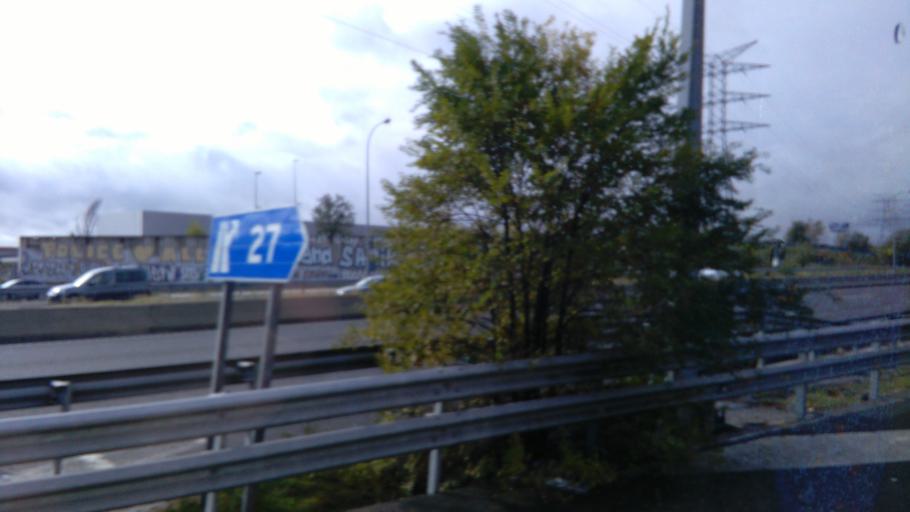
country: ES
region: Madrid
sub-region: Provincia de Madrid
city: Latina
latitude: 40.3622
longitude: -3.7392
